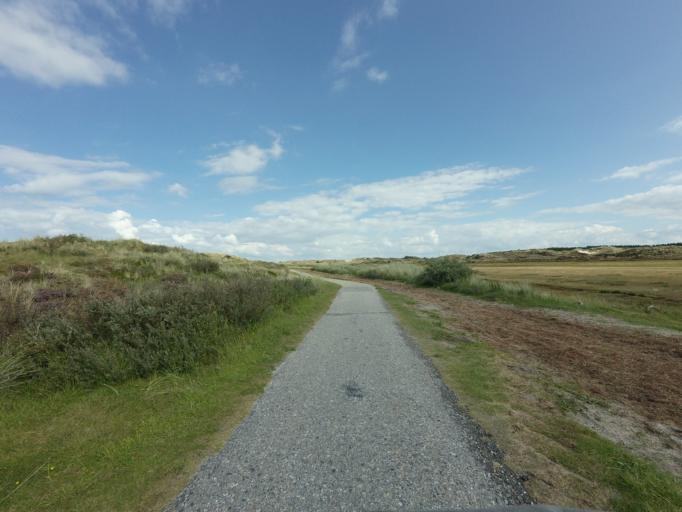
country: NL
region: Friesland
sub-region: Gemeente Terschelling
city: West-Terschelling
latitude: 53.3947
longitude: 5.2684
